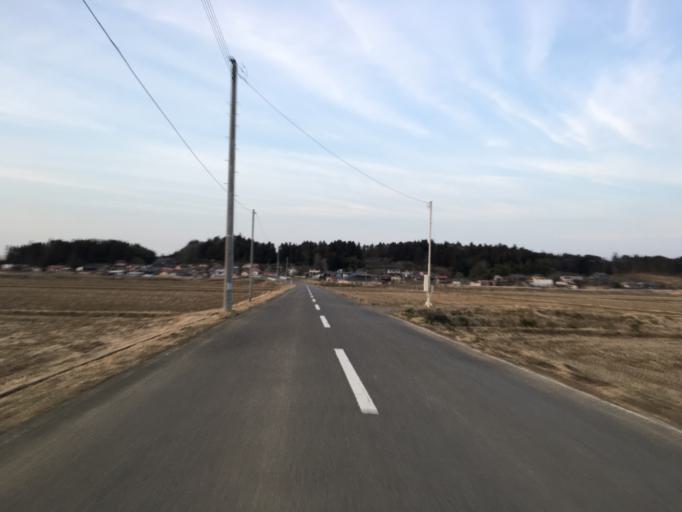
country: JP
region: Fukushima
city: Ishikawa
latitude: 37.0605
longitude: 140.3483
